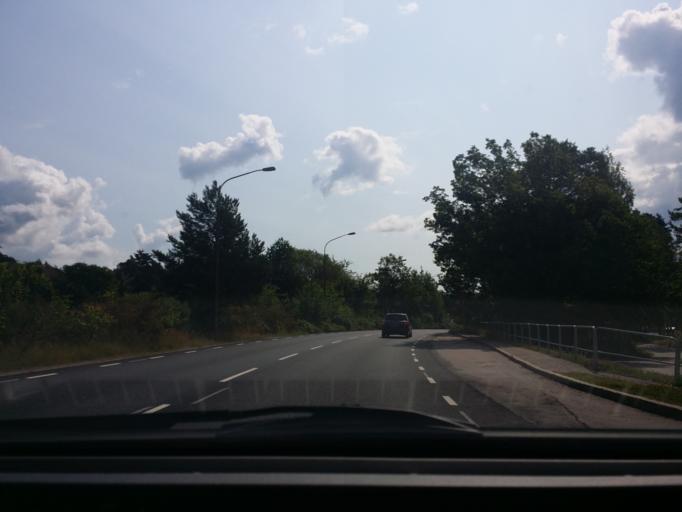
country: SE
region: Vaestmanland
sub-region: Vasteras
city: Vasteras
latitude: 59.6064
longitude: 16.5917
